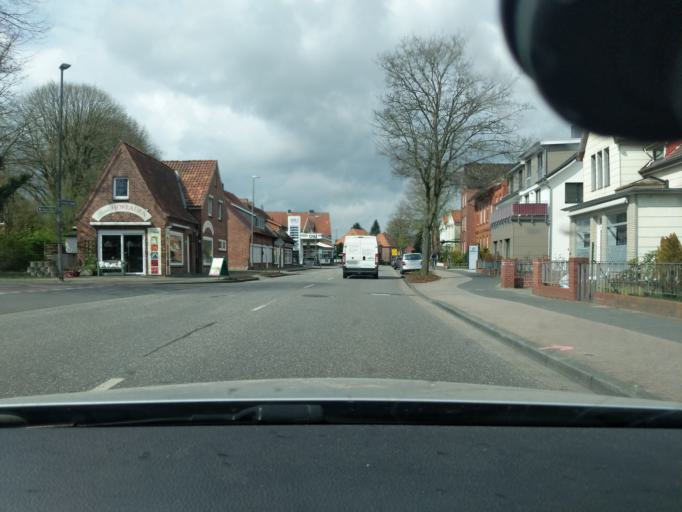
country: DE
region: Lower Saxony
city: Stade
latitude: 53.5934
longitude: 9.4788
